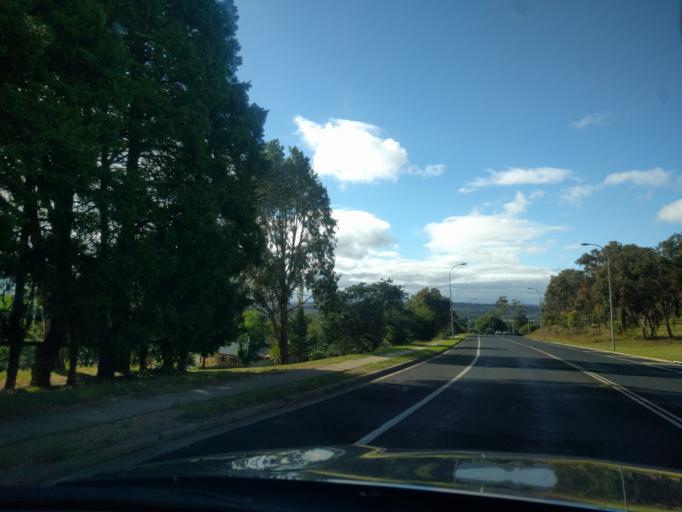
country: AU
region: New South Wales
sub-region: Armidale Dumaresq
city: Armidale
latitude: -30.4961
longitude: 151.6700
